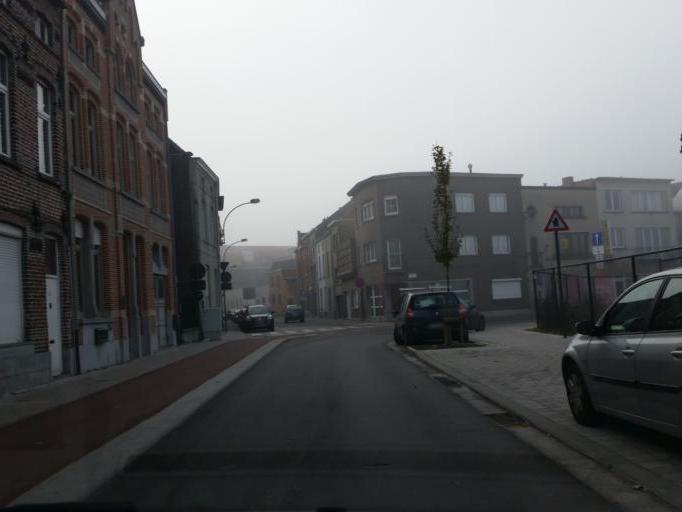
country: BE
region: Flanders
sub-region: Provincie Oost-Vlaanderen
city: Aalst
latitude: 50.9464
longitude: 4.0407
